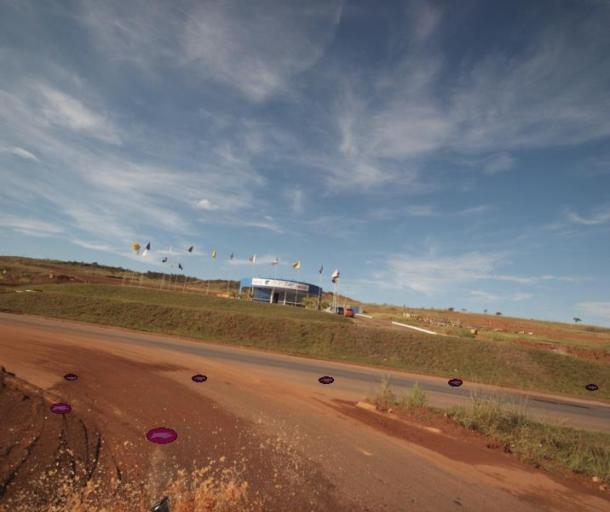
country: BR
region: Federal District
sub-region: Brasilia
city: Brasilia
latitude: -15.7554
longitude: -48.3375
